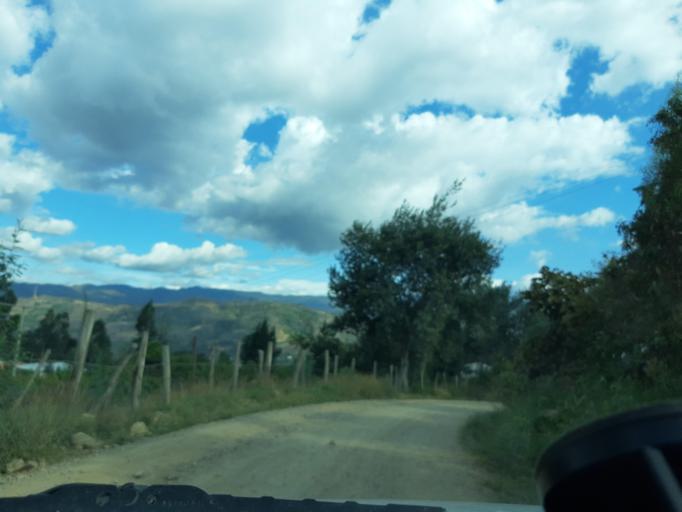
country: CO
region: Boyaca
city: Raquira
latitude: 5.5337
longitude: -73.6467
